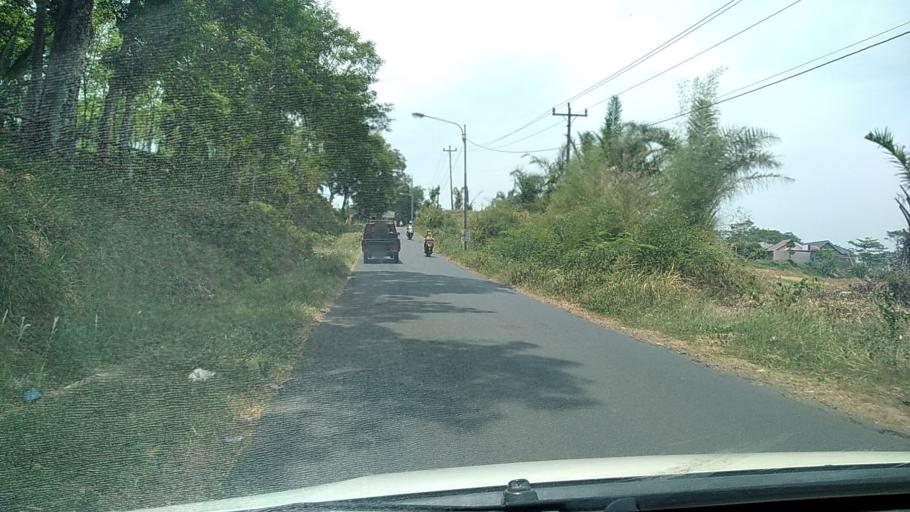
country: ID
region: Central Java
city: Ungaran
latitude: -7.0935
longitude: 110.3078
